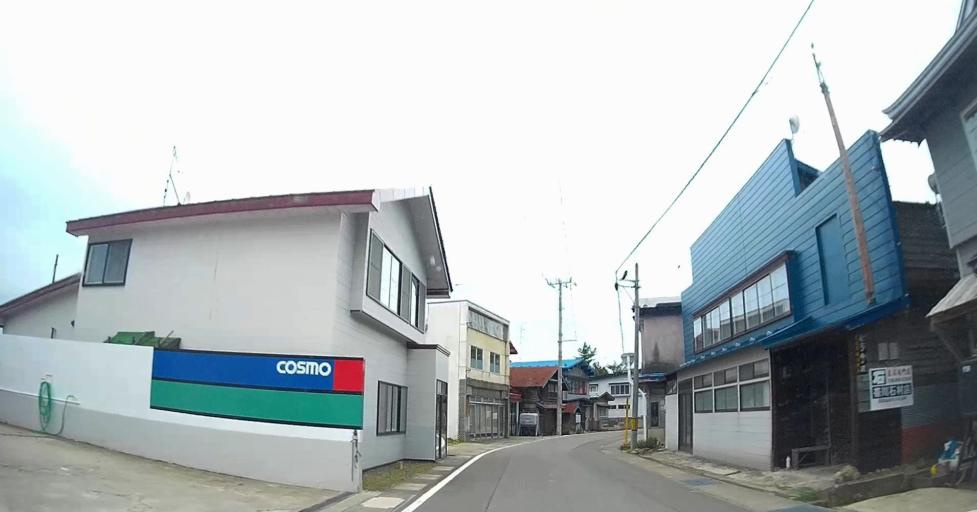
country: JP
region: Aomori
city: Shimokizukuri
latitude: 41.2009
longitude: 140.4295
